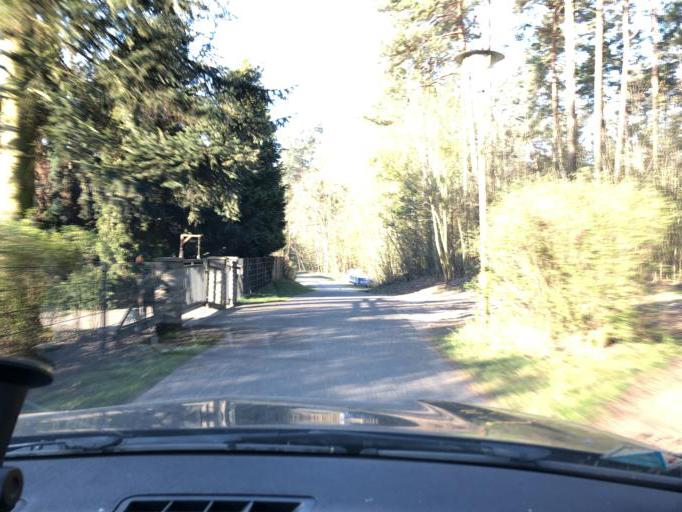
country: DE
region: Saxony
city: Krauschwitz
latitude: 51.5144
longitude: 14.7099
